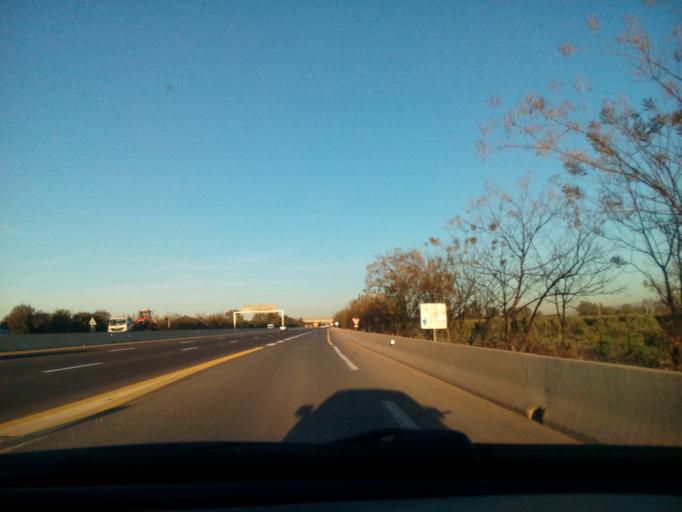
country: DZ
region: Relizane
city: Oued Rhiou
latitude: 35.9692
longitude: 0.9005
